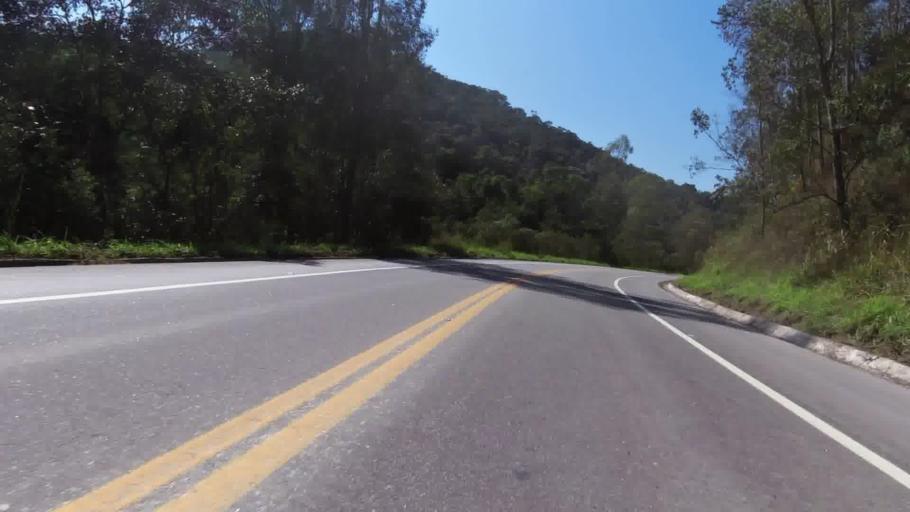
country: BR
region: Espirito Santo
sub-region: Marechal Floriano
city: Marechal Floriano
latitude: -20.4133
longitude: -40.8543
